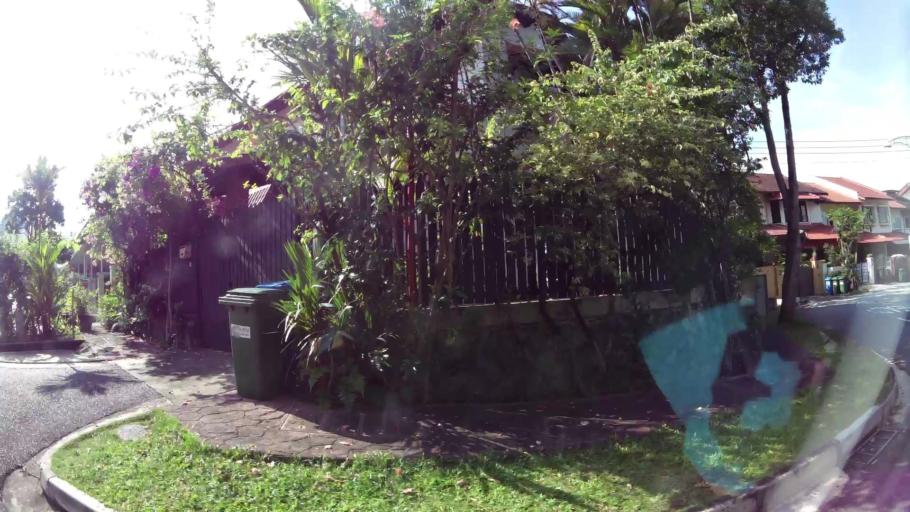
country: SG
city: Singapore
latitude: 1.3545
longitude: 103.8375
